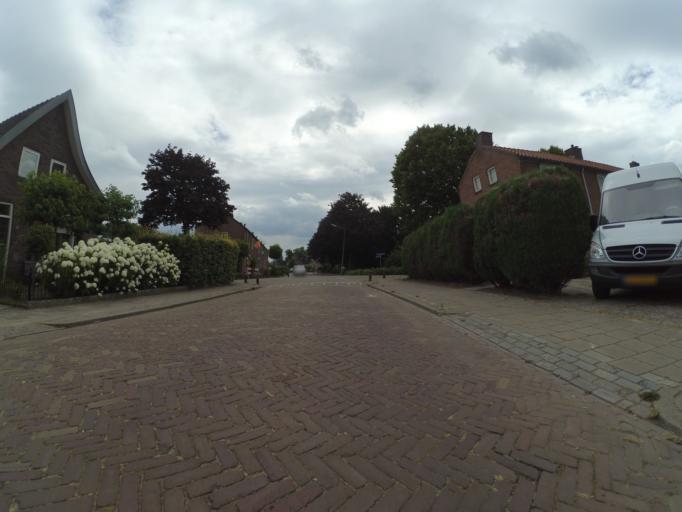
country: NL
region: Gelderland
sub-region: Gemeente Brummen
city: Eerbeek
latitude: 52.1006
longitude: 6.0595
